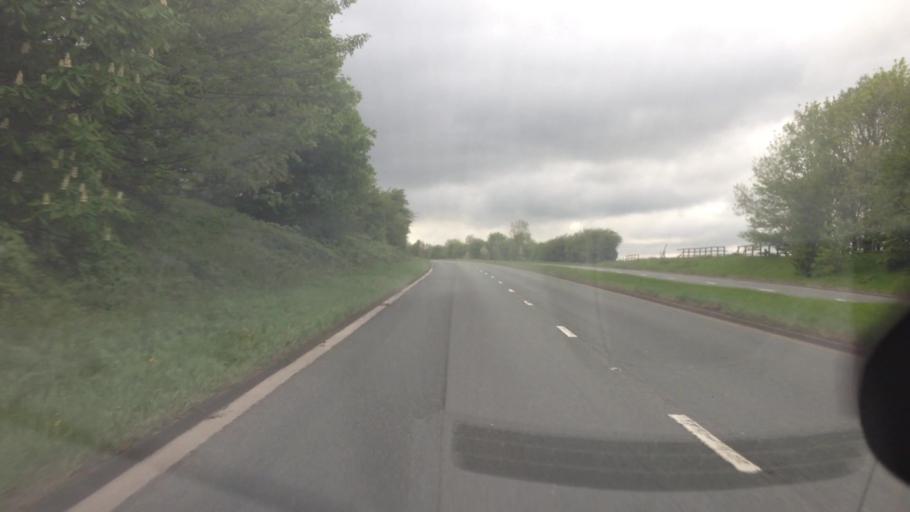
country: GB
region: England
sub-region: City and Borough of Wakefield
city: Ossett
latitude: 53.6908
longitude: -1.5780
